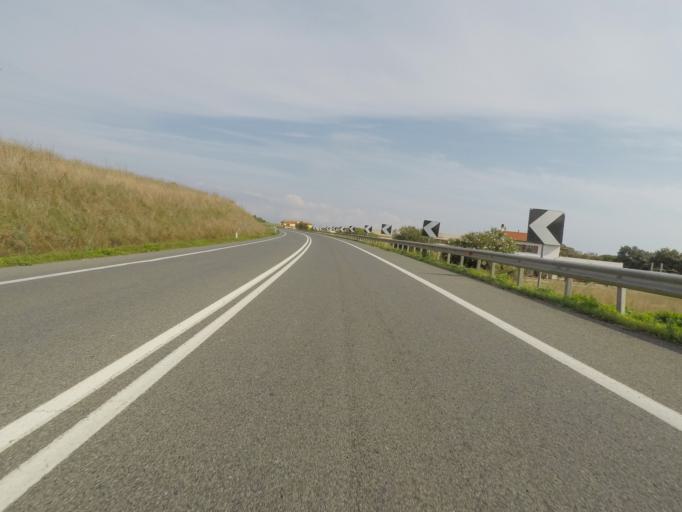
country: IT
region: Tuscany
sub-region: Provincia di Grosseto
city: Orbetello Scalo
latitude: 42.4143
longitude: 11.3358
